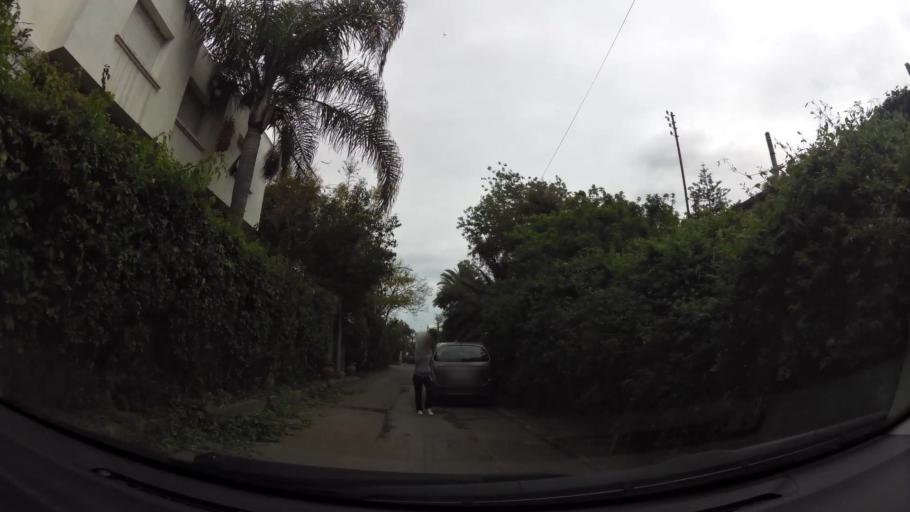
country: MA
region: Grand Casablanca
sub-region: Casablanca
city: Casablanca
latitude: 33.5734
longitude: -7.6554
